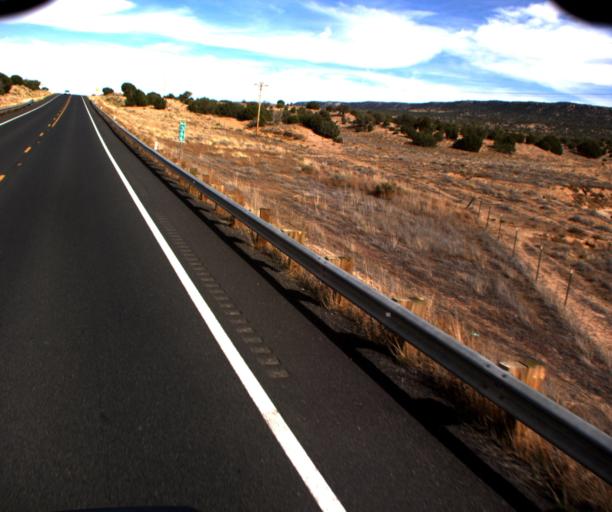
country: US
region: Arizona
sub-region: Navajo County
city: Kayenta
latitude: 36.4949
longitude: -110.6261
